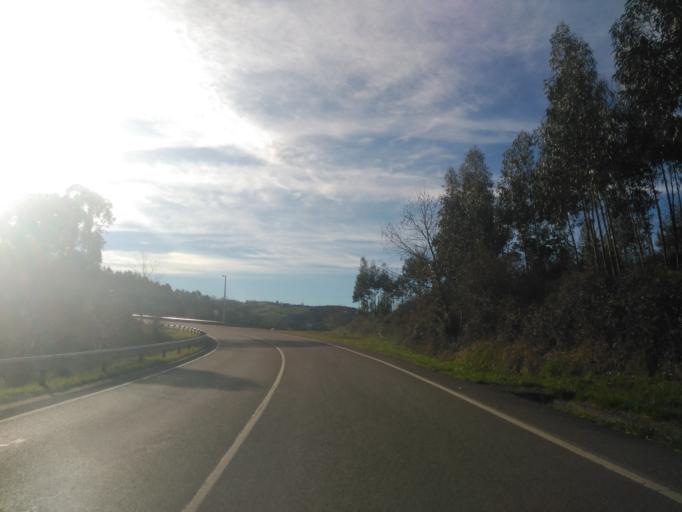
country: ES
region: Cantabria
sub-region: Provincia de Cantabria
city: Comillas
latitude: 43.3664
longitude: -4.2768
